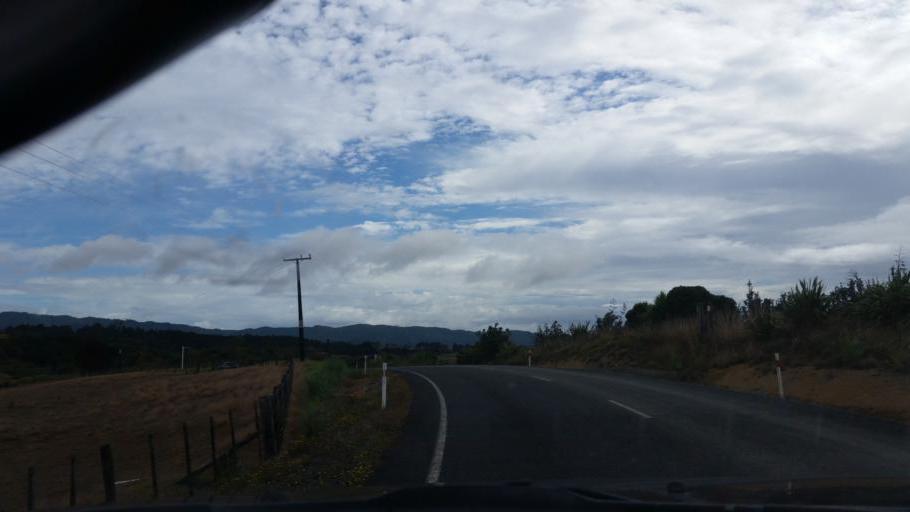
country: NZ
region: Auckland
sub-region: Auckland
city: Wellsford
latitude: -36.1486
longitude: 174.5447
